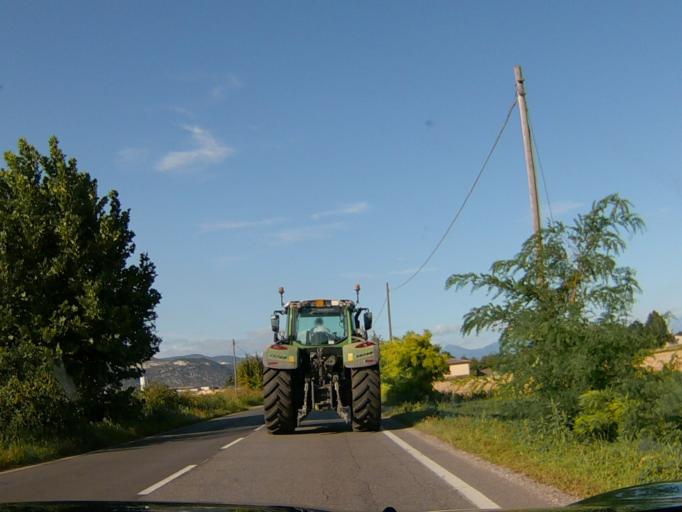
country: IT
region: Lombardy
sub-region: Provincia di Brescia
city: Molinetto
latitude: 45.4859
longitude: 10.3364
